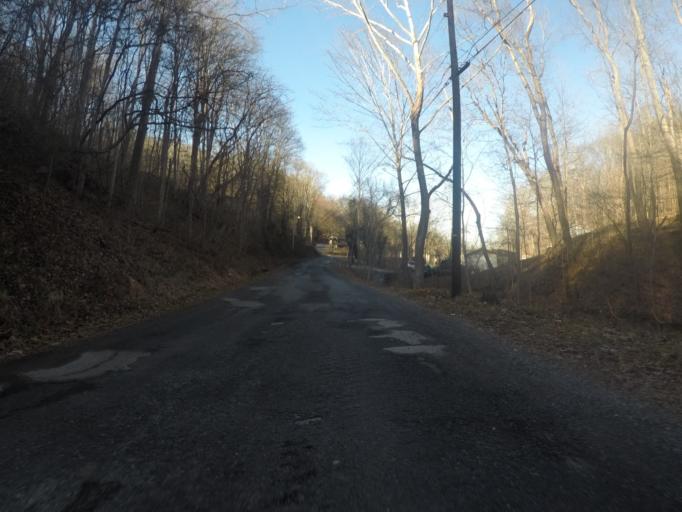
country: US
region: West Virginia
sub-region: Cabell County
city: Huntington
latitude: 38.3947
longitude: -82.4871
